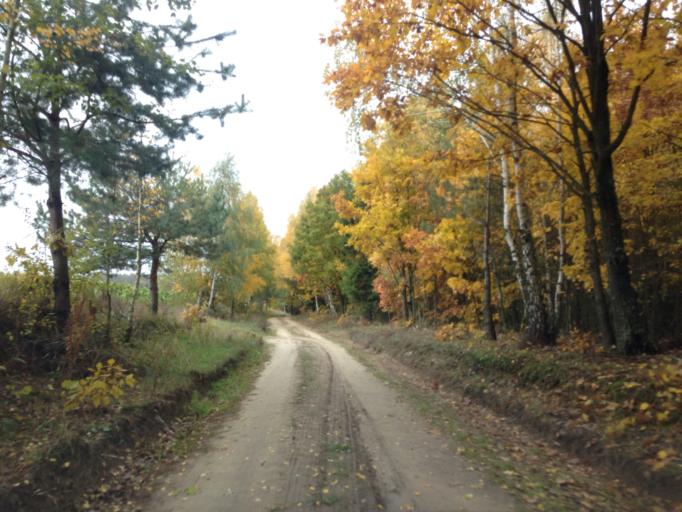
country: PL
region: Kujawsko-Pomorskie
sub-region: Powiat brodnicki
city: Gorzno
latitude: 53.2721
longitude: 19.7078
